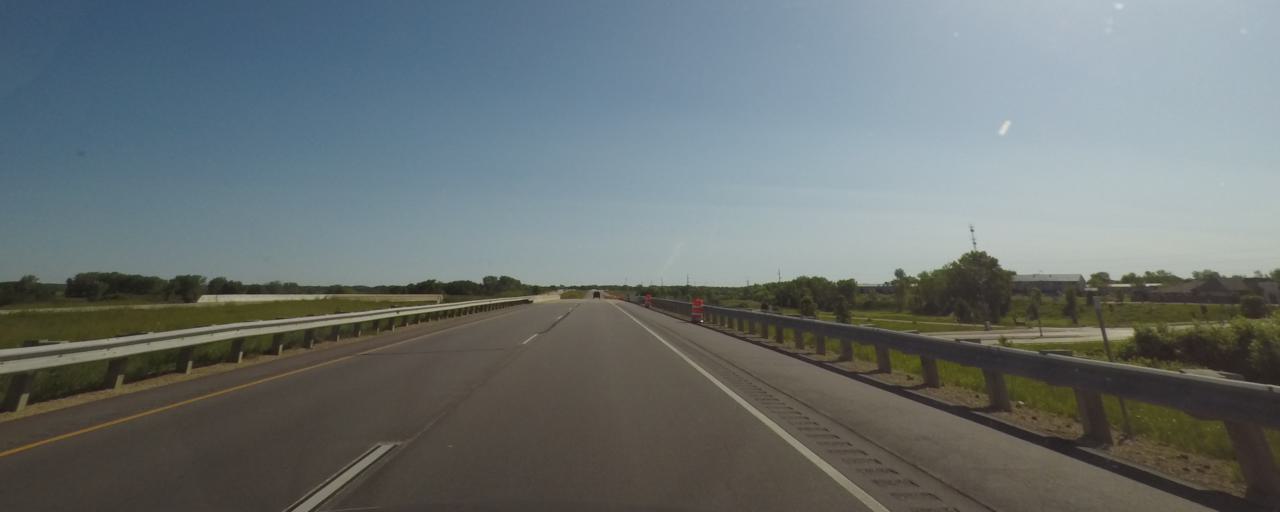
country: US
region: Wisconsin
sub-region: Columbia County
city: Columbus
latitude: 43.3466
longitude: -89.0352
